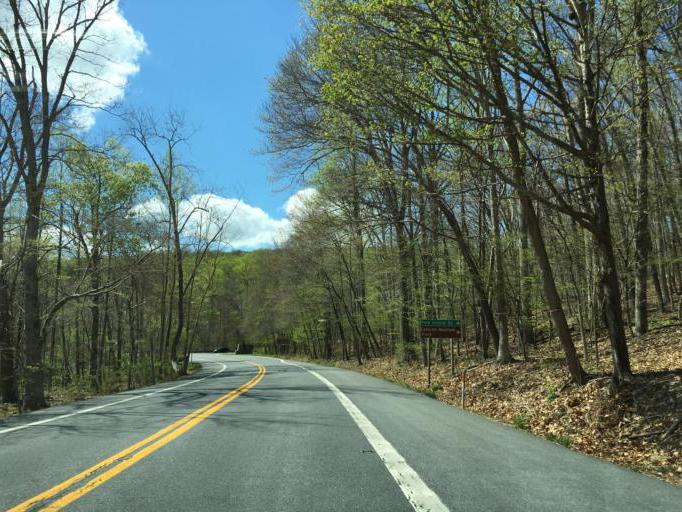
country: US
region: Maryland
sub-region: Frederick County
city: Thurmont
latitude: 39.6330
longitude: -77.4483
